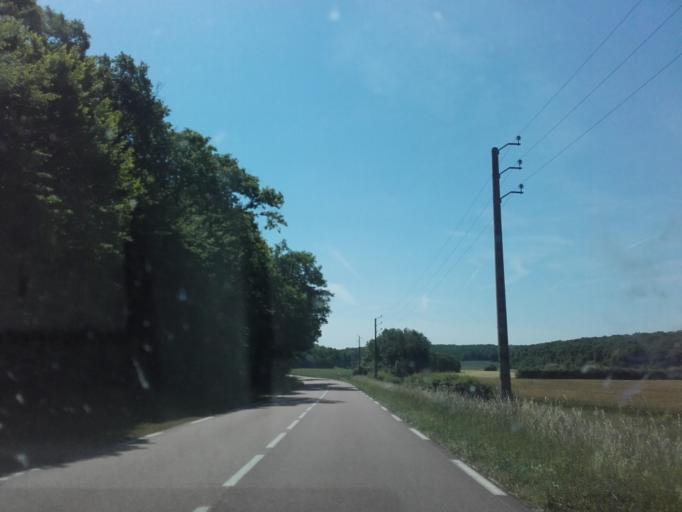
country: FR
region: Bourgogne
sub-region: Departement de l'Yonne
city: Chablis
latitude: 47.7526
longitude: 3.8227
